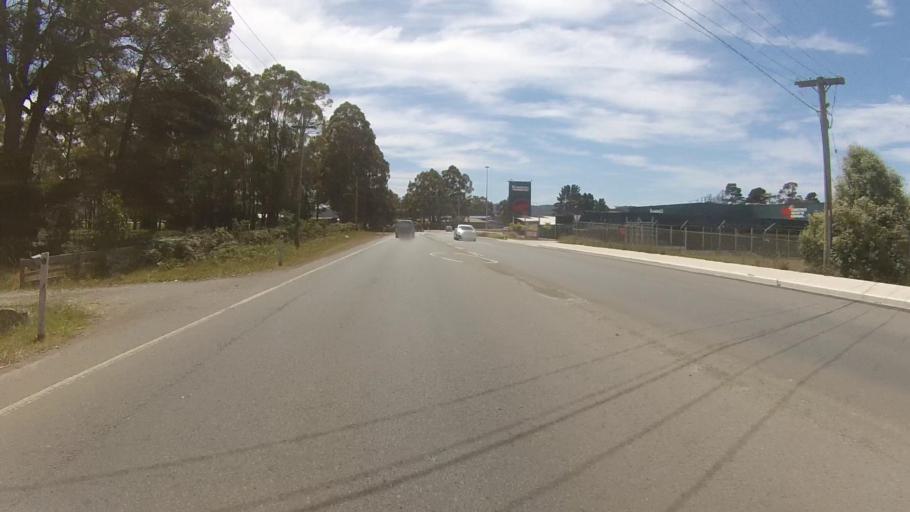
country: AU
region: Tasmania
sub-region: Kingborough
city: Kingston
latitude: -42.9854
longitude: 147.2911
